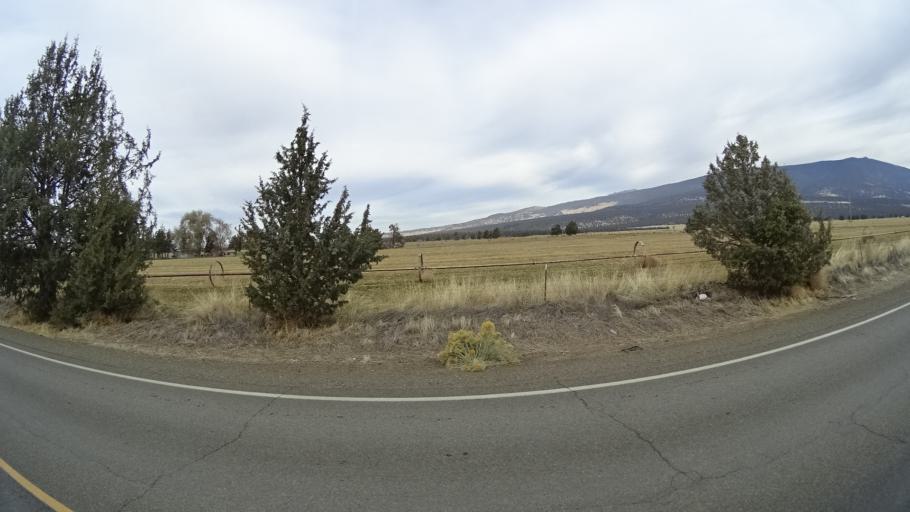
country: US
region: California
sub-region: Siskiyou County
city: Weed
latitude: 41.5958
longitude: -122.3327
